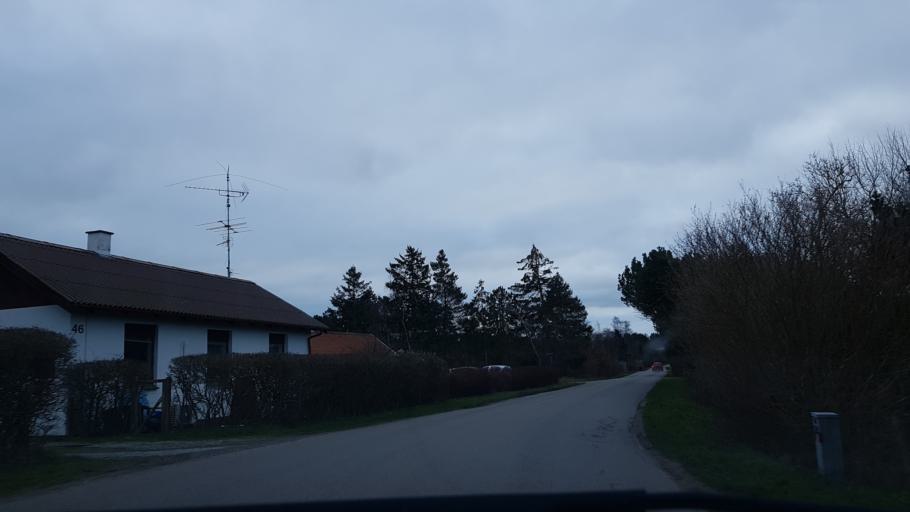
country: DK
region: Zealand
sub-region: Odsherred Kommune
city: Hojby
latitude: 55.9418
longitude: 11.6115
